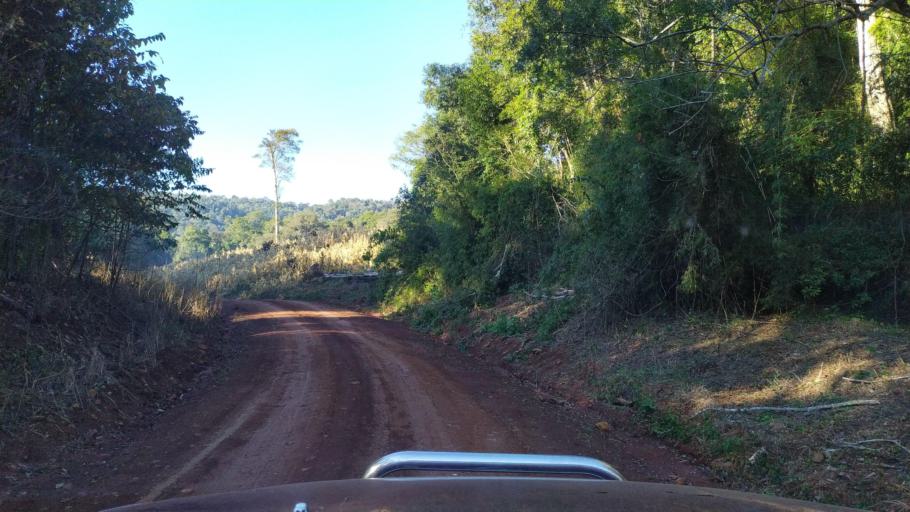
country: AR
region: Misiones
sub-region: Departamento de Montecarlo
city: Montecarlo
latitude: -26.6973
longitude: -54.5662
